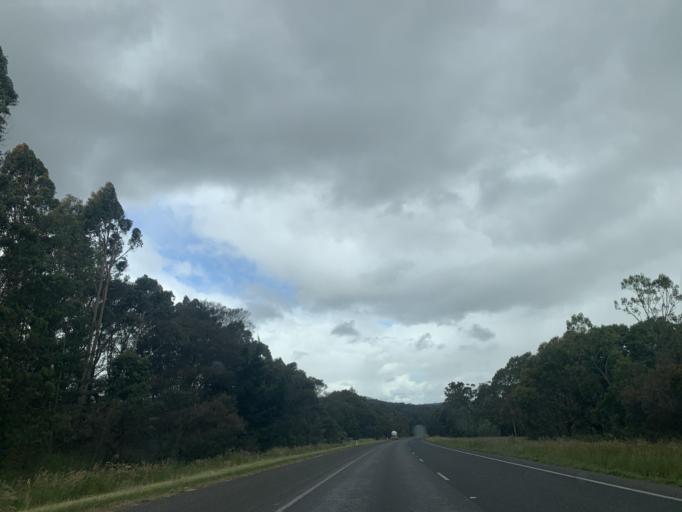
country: AU
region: Victoria
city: Brown Hill
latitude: -37.5386
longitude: 143.8835
